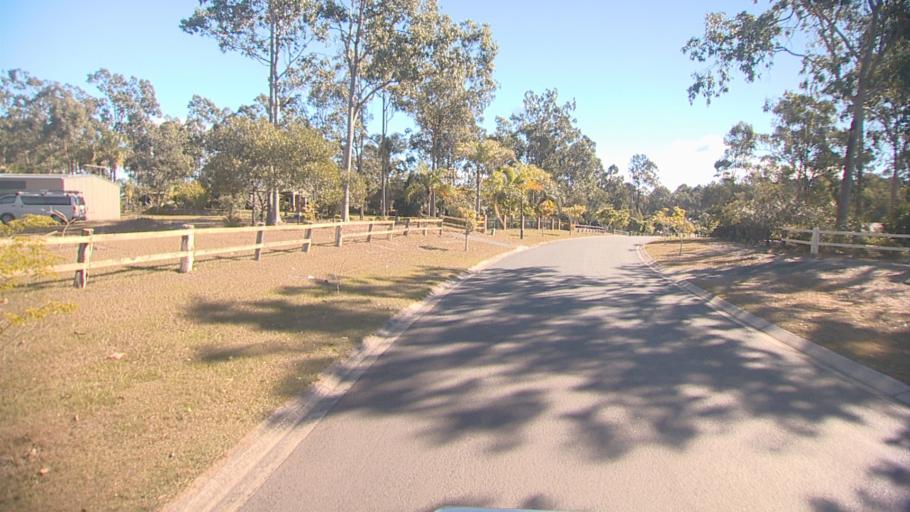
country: AU
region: Queensland
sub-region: Ipswich
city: Springfield Lakes
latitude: -27.7265
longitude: 152.9220
